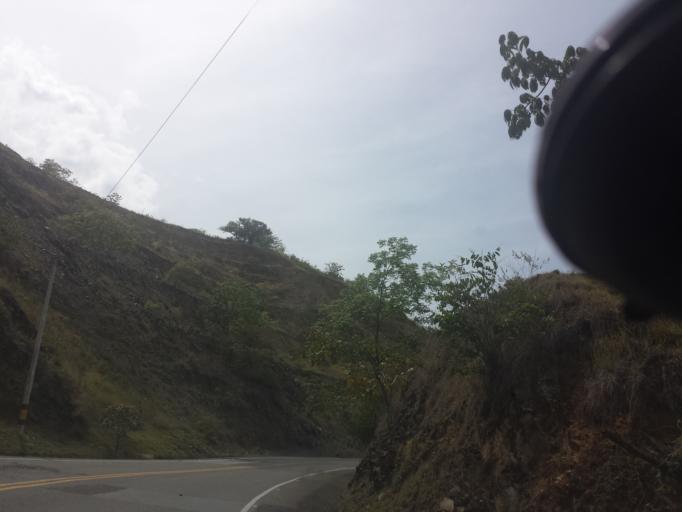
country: CO
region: Antioquia
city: Antioquia
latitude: 6.5787
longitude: -75.8375
